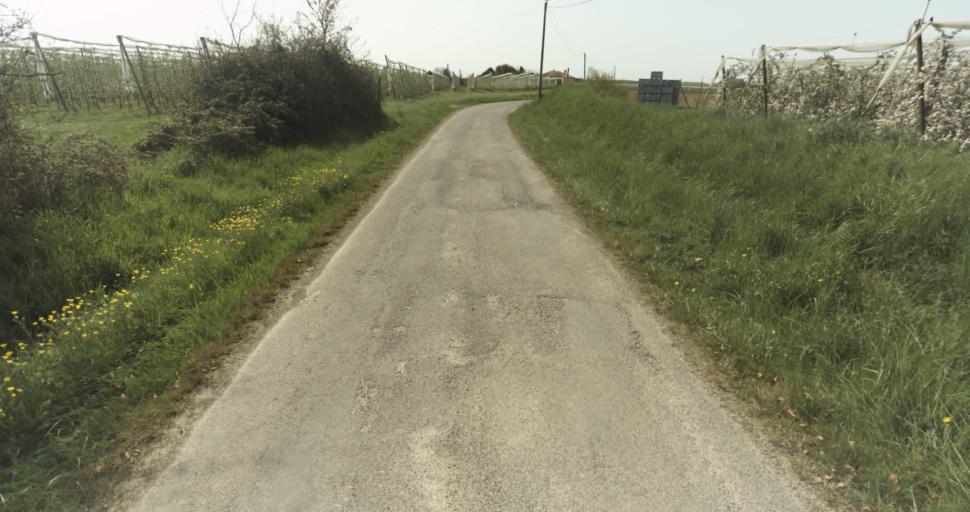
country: FR
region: Midi-Pyrenees
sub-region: Departement du Tarn-et-Garonne
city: Moissac
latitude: 44.0934
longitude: 1.0697
